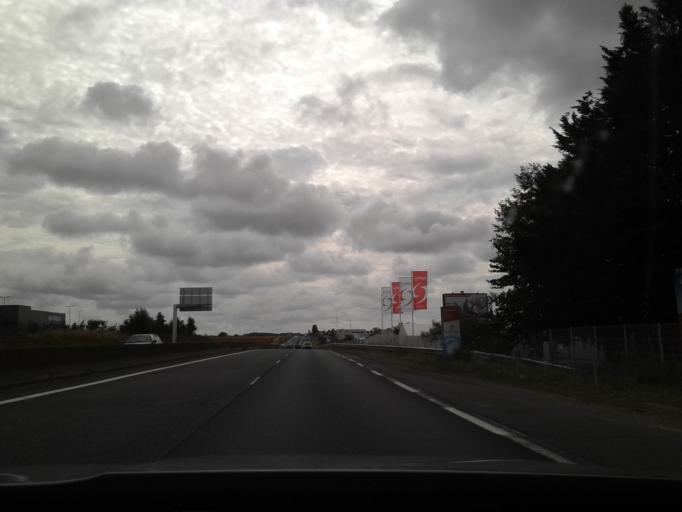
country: FR
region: Lower Normandy
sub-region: Departement du Calvados
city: Carpiquet
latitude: 49.1963
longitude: -0.4563
